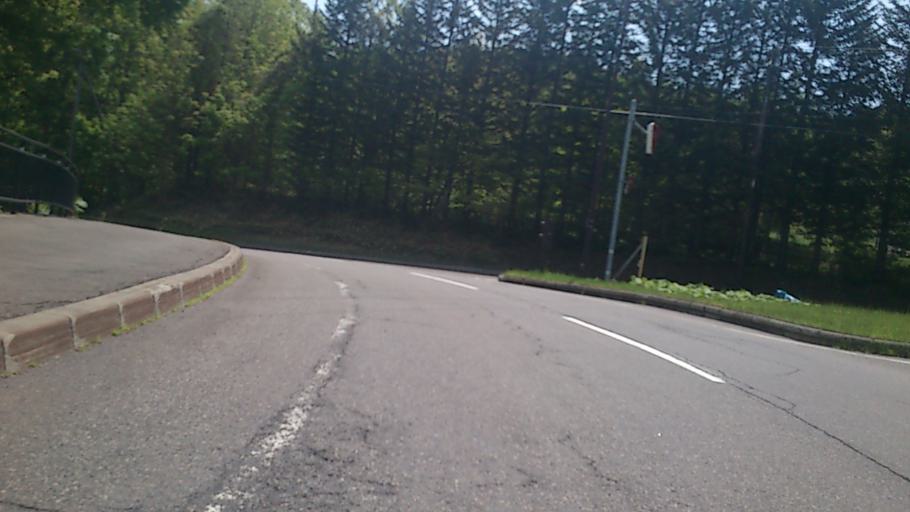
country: JP
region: Hokkaido
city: Otofuke
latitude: 43.3650
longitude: 143.1855
